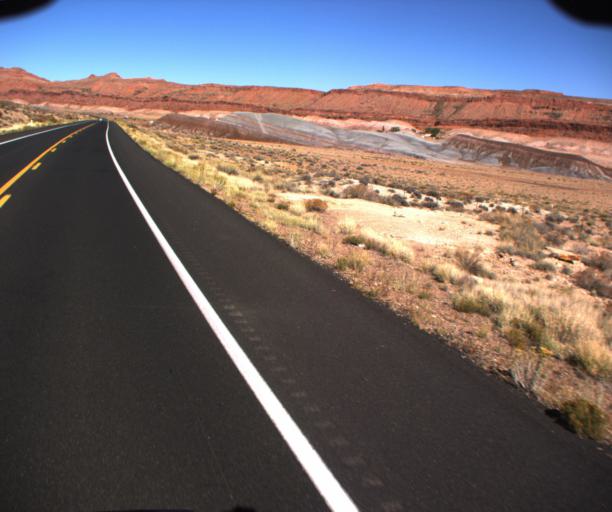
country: US
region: Arizona
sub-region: Coconino County
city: Tuba City
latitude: 36.1791
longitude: -111.3987
